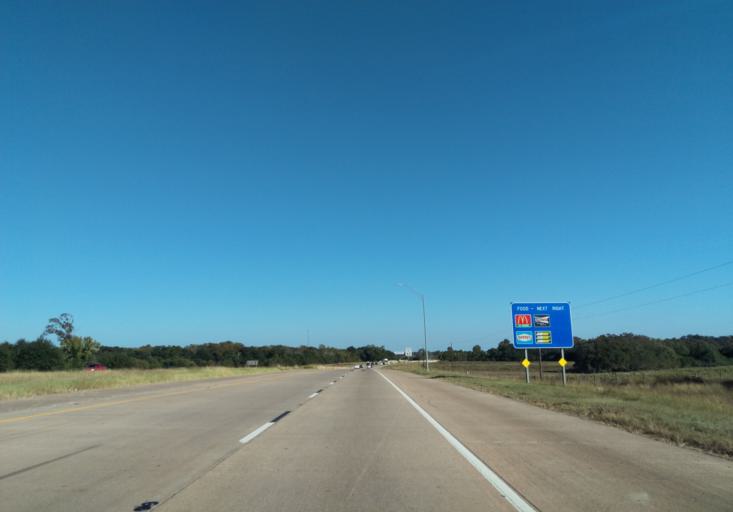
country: US
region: Texas
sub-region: Waller County
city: Hempstead
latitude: 30.1127
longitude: -96.0615
